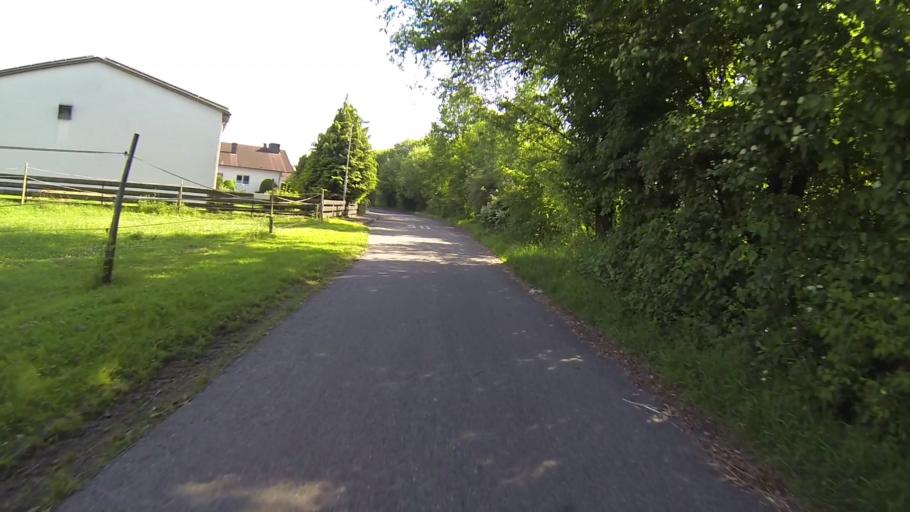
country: DE
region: Baden-Wuerttemberg
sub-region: Tuebingen Region
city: Laupheim
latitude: 48.1920
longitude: 9.8274
